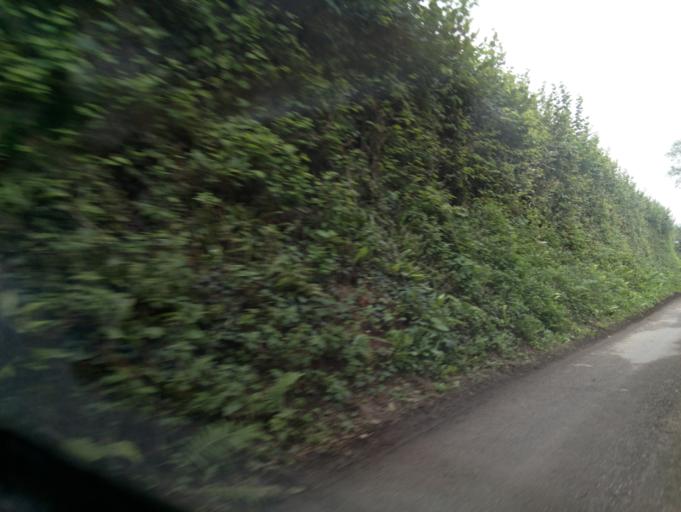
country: GB
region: England
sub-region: Devon
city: Kingsbridge
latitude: 50.2930
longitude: -3.7174
